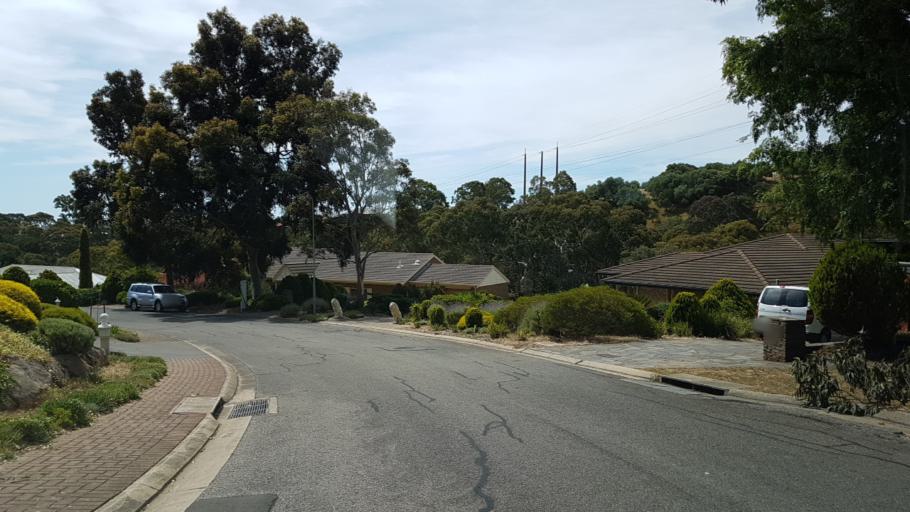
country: AU
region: South Australia
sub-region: Burnside
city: Wattle Park
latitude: -34.9142
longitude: 138.6882
